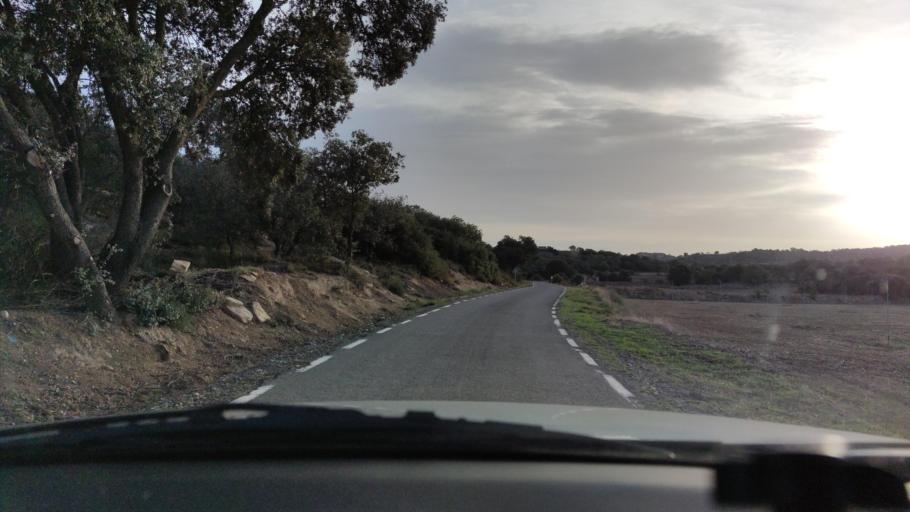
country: ES
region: Catalonia
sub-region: Provincia de Lleida
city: Agramunt
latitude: 41.8368
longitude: 1.0727
